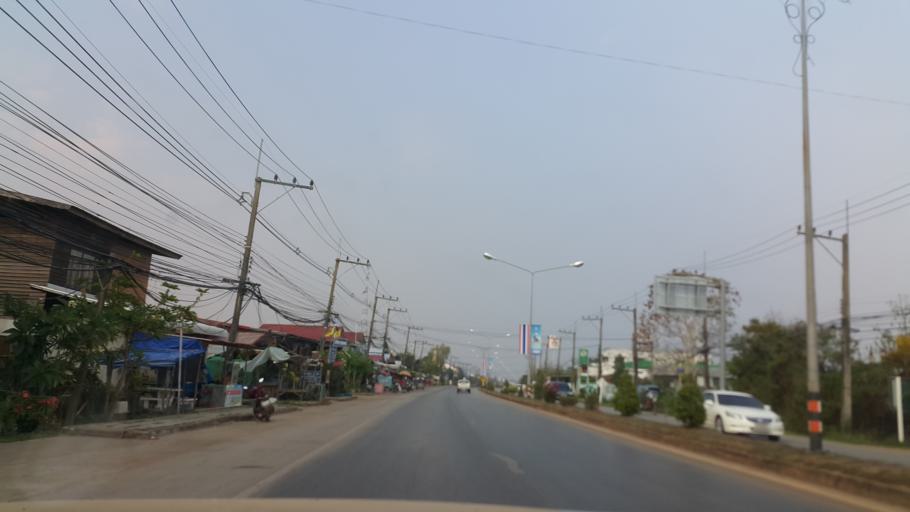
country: TH
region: Nakhon Phanom
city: That Phanom
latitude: 16.9587
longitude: 104.7256
